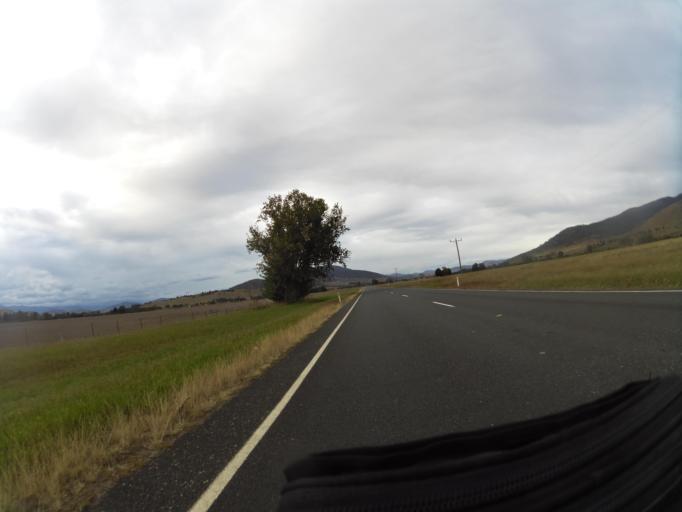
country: AU
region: New South Wales
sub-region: Snowy River
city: Jindabyne
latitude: -36.1057
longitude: 147.9803
